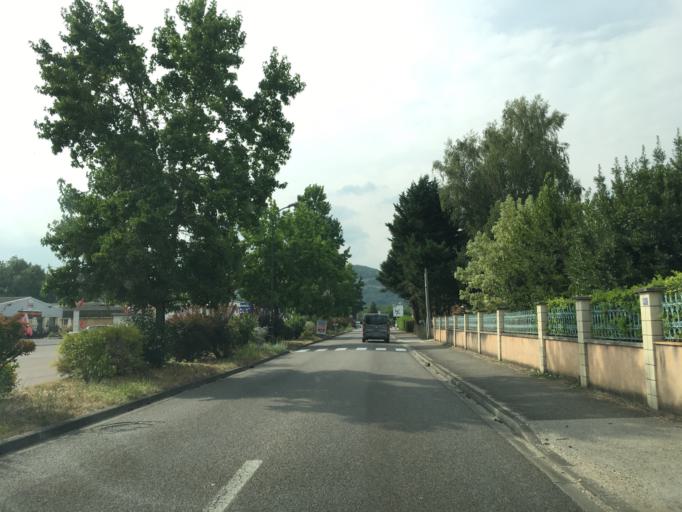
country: FR
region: Midi-Pyrenees
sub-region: Departement du Lot
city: Souillac
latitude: 44.8965
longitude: 1.4651
